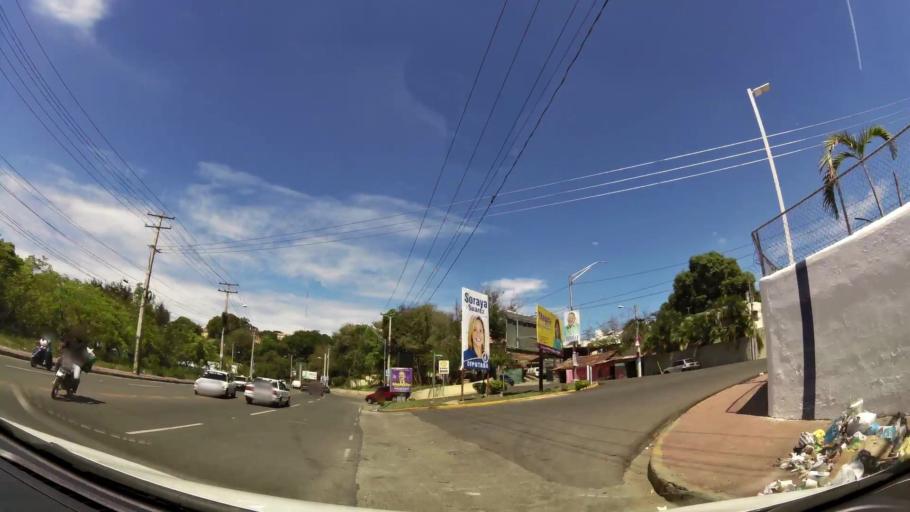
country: DO
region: Santiago
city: Santiago de los Caballeros
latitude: 19.4445
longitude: -70.7031
